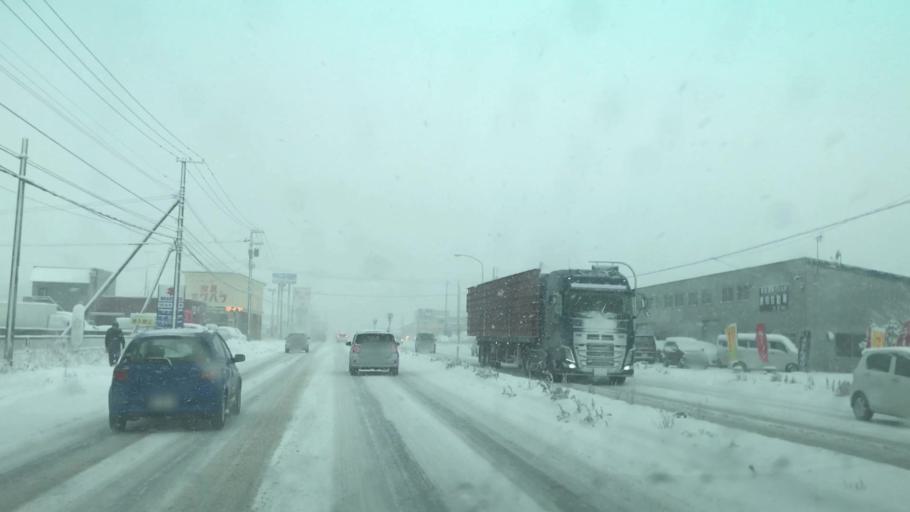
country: JP
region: Hokkaido
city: Muroran
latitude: 42.3844
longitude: 141.0769
